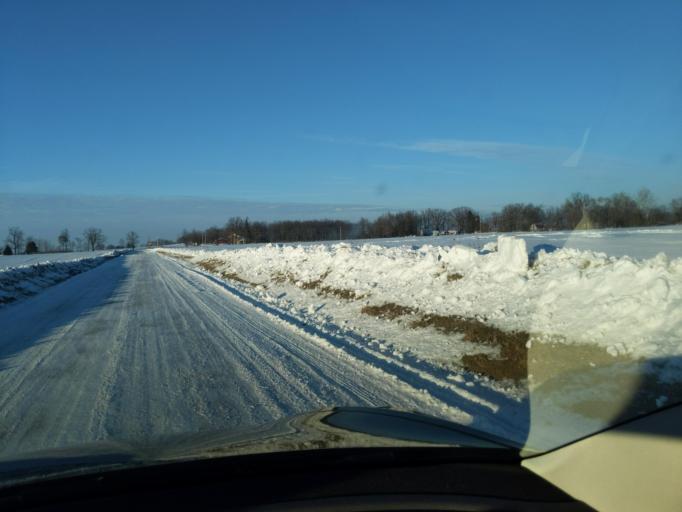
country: US
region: Michigan
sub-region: Ingham County
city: Stockbridge
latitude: 42.4929
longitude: -84.1194
